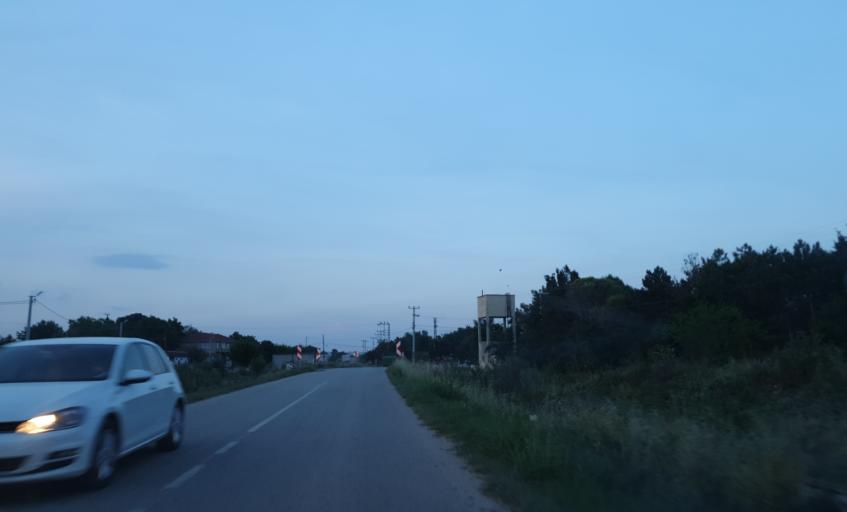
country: TR
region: Tekirdag
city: Beyazkoy
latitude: 41.4385
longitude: 27.6982
